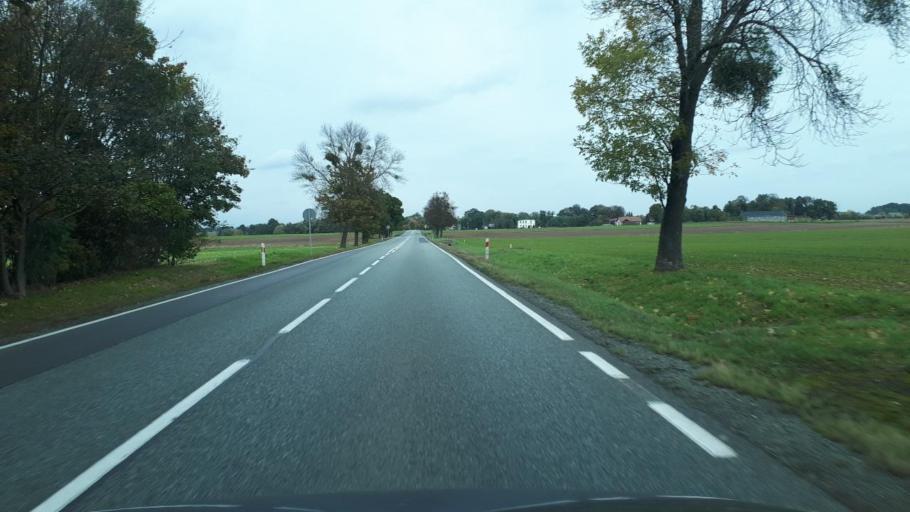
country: PL
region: Opole Voivodeship
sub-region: Powiat kluczborski
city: Byczyna
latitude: 51.0558
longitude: 18.1980
